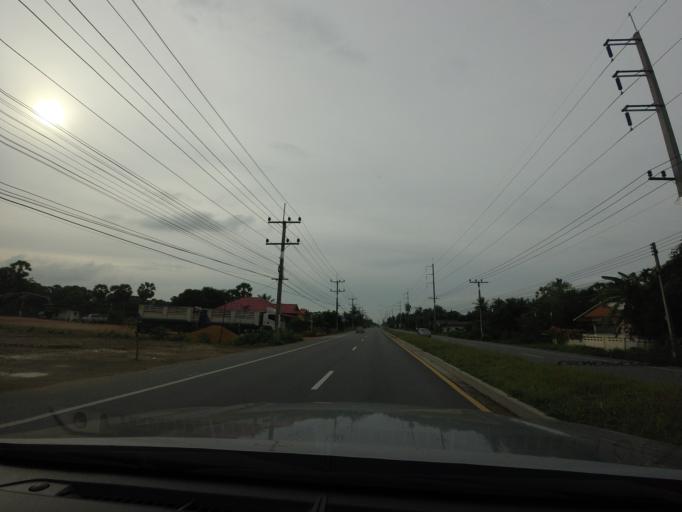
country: TH
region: Songkhla
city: Ranot
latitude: 7.7002
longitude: 100.3752
